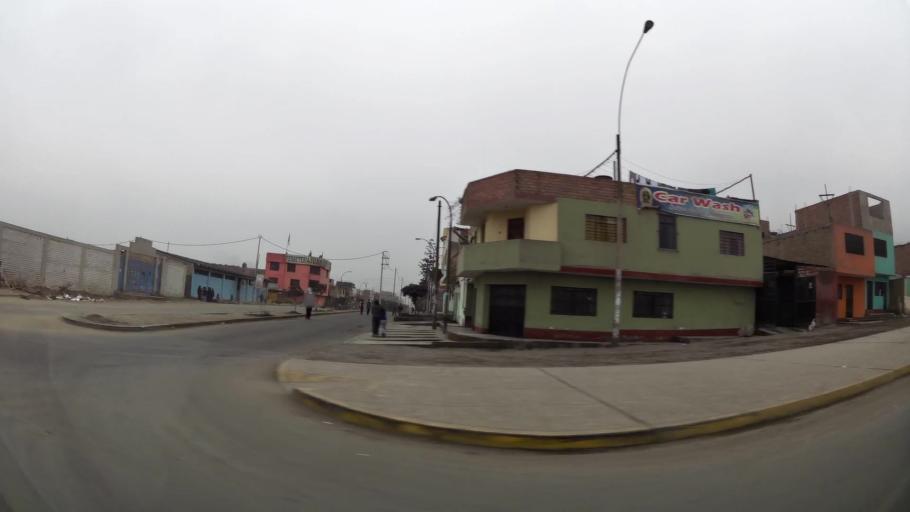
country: PE
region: Lima
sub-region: Lima
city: Urb. Santo Domingo
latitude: -11.8729
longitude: -77.0167
